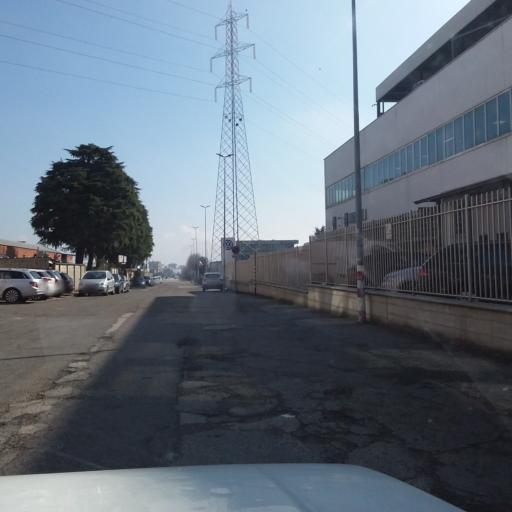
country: IT
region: Piedmont
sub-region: Provincia di Torino
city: Tetti Neirotti
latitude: 45.0635
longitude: 7.5480
